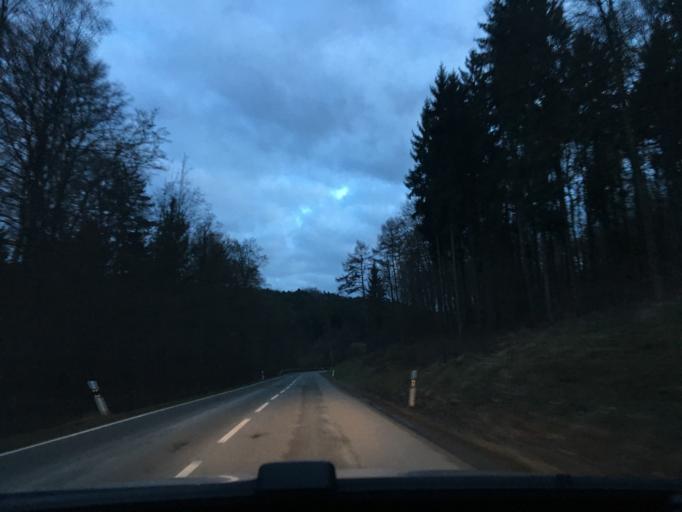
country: DE
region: Rheinland-Pfalz
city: Oberwiesen
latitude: 49.6809
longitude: 7.9727
